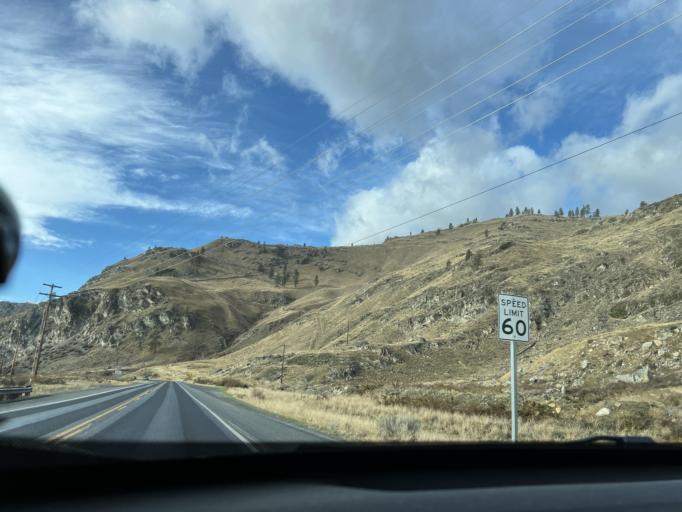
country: US
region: Washington
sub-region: Chelan County
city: Chelan
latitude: 47.8609
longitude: -119.9518
